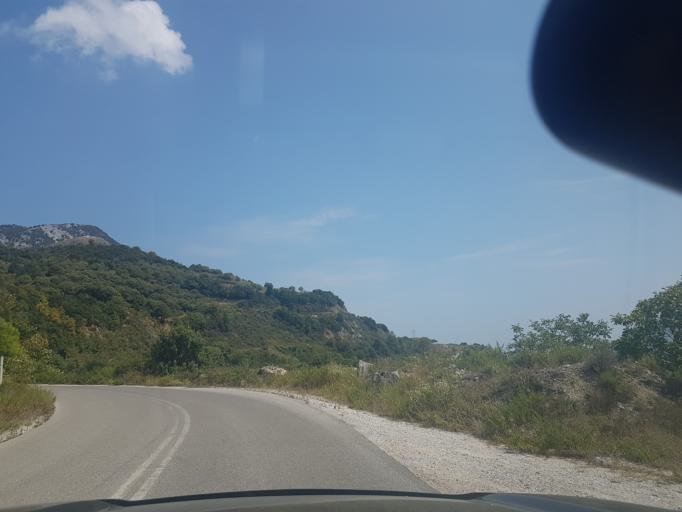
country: GR
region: Central Greece
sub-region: Nomos Evvoias
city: Yimnon
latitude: 38.6415
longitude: 23.8958
